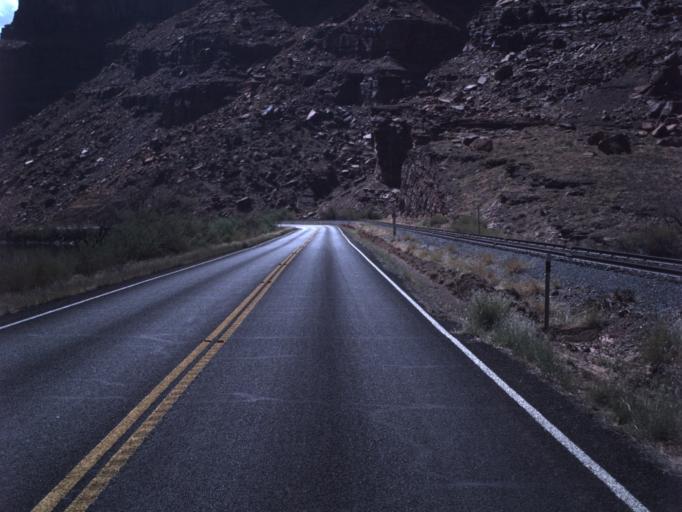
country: US
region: Utah
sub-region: Grand County
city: Moab
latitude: 38.5443
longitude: -109.6505
